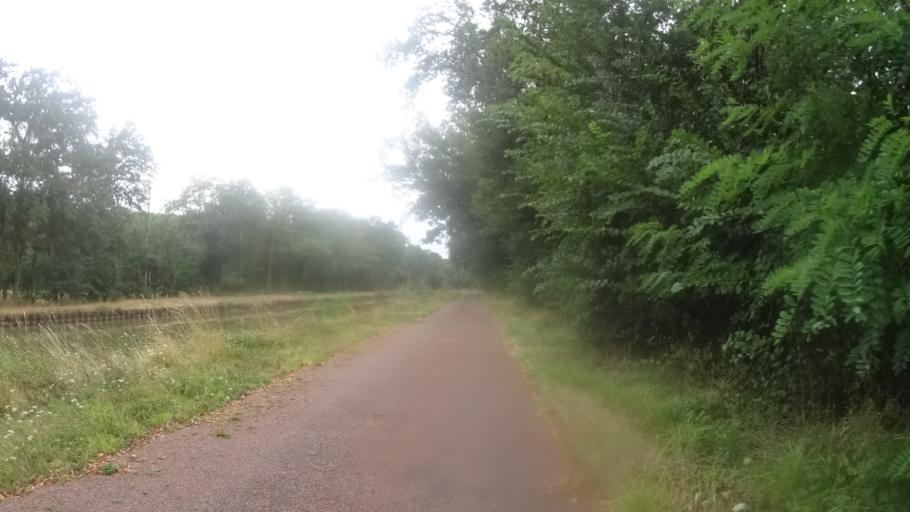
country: FR
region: Bourgogne
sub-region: Departement de la Nievre
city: Imphy
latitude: 46.8784
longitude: 3.2625
